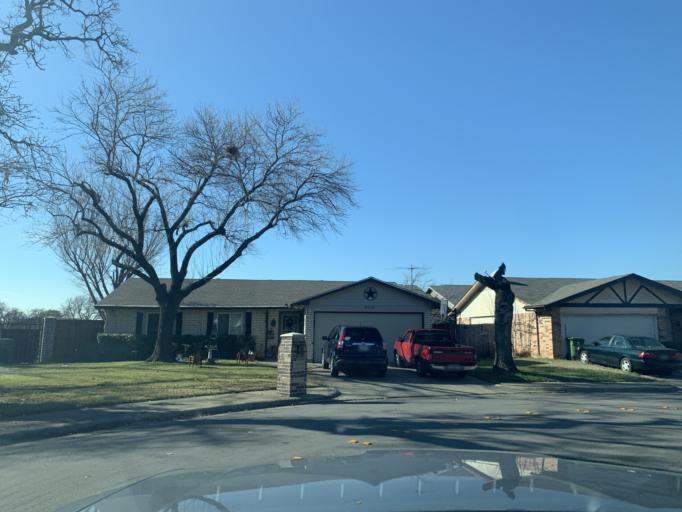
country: US
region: Texas
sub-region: Tarrant County
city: Bedford
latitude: 32.8426
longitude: -97.1488
